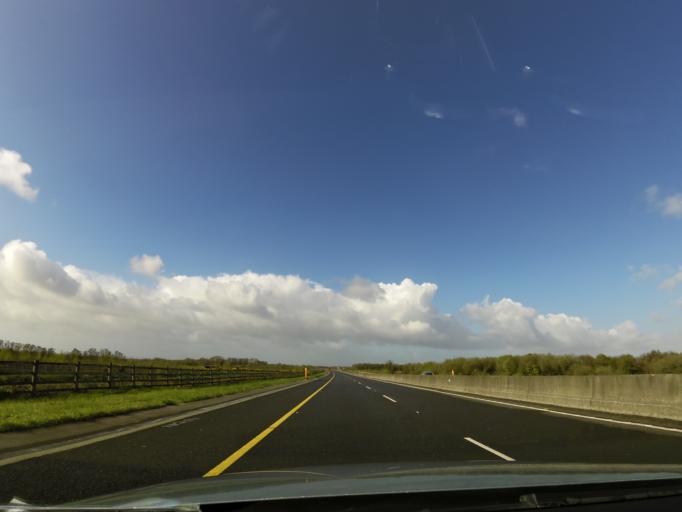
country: IE
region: Munster
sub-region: County Limerick
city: Castleconnell
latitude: 52.7296
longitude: -8.4601
